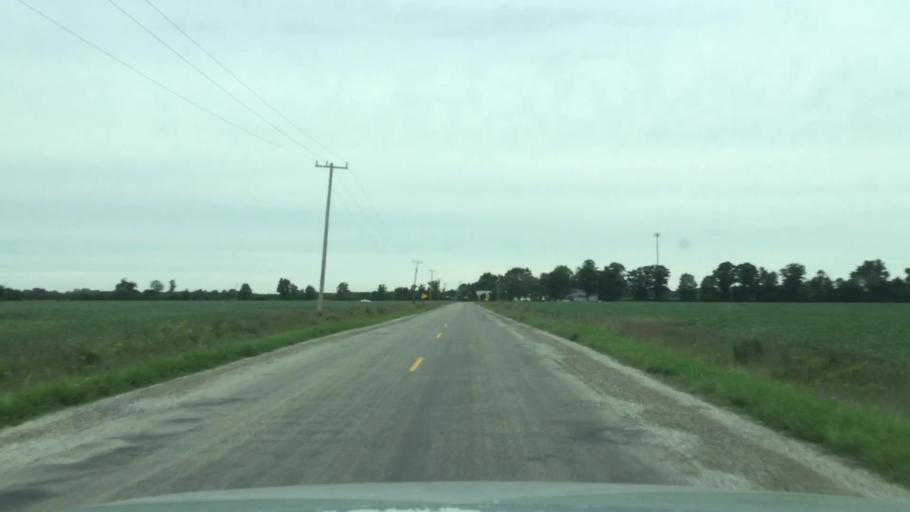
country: US
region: Michigan
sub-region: Washtenaw County
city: Milan
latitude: 42.0788
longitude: -83.7357
